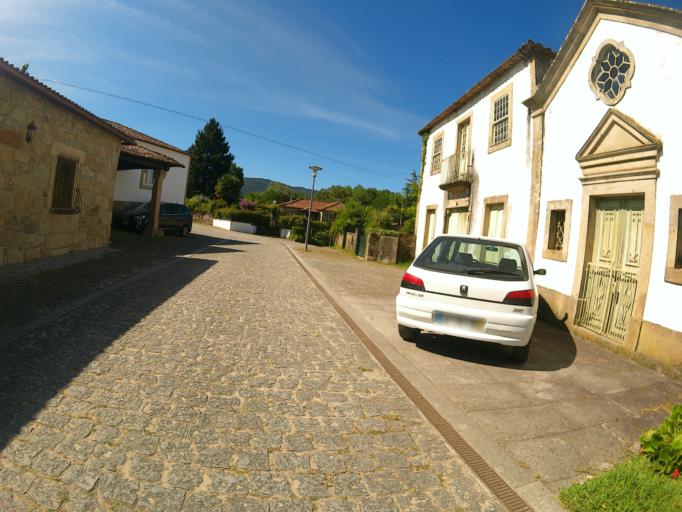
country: PT
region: Viana do Castelo
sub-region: Viana do Castelo
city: Darque
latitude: 41.7237
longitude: -8.6760
